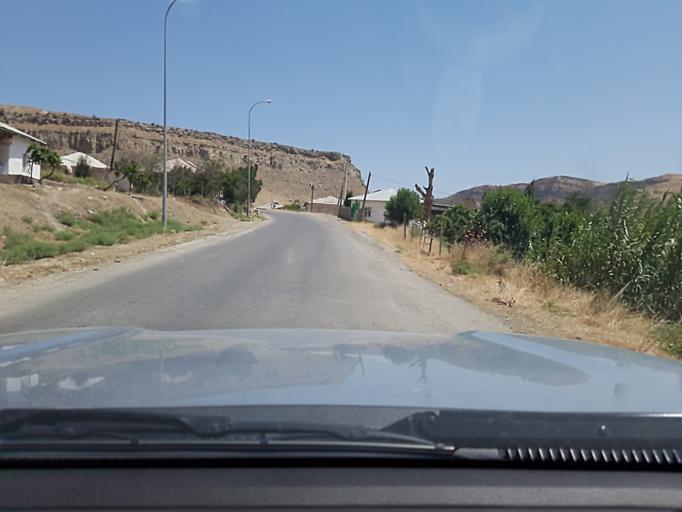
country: TM
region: Balkan
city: Magtymguly
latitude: 38.4318
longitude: 56.5860
